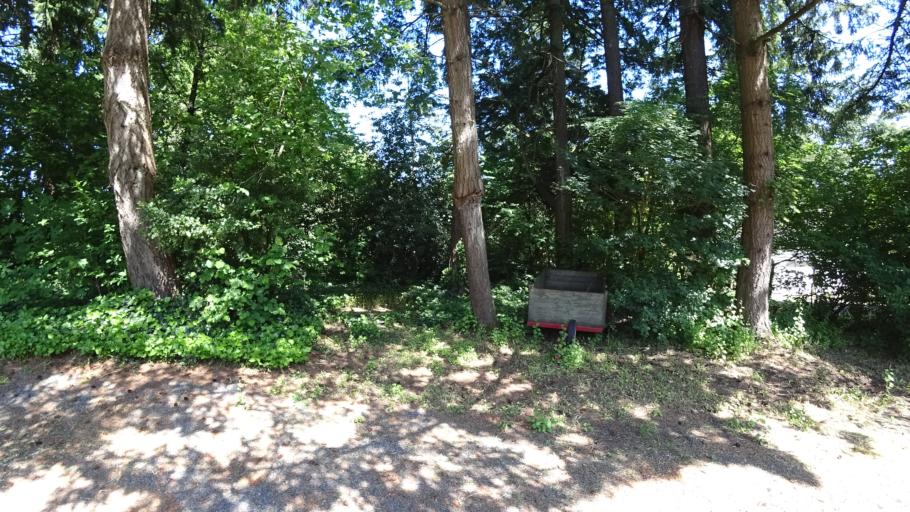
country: US
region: Oregon
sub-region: Washington County
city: Metzger
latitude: 45.4472
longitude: -122.7151
